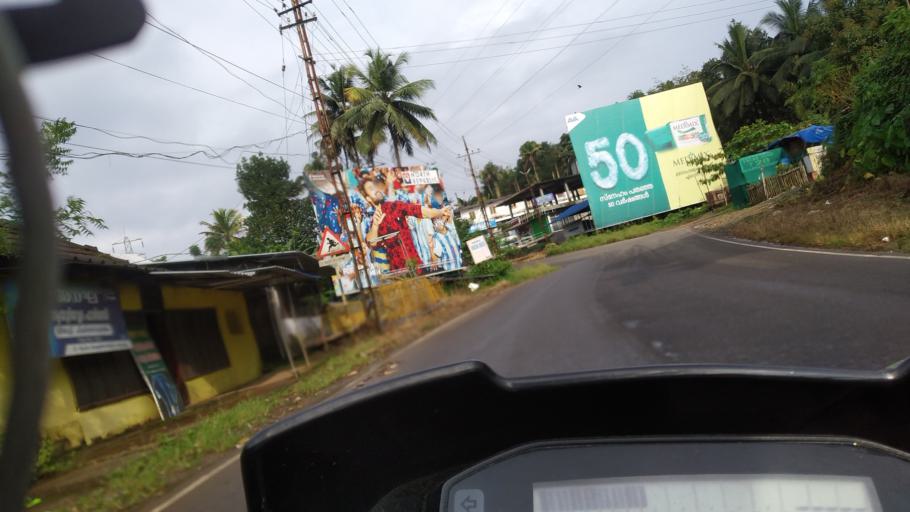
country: IN
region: Kerala
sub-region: Ernakulam
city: Kotamangalam
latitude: 10.0511
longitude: 76.7147
